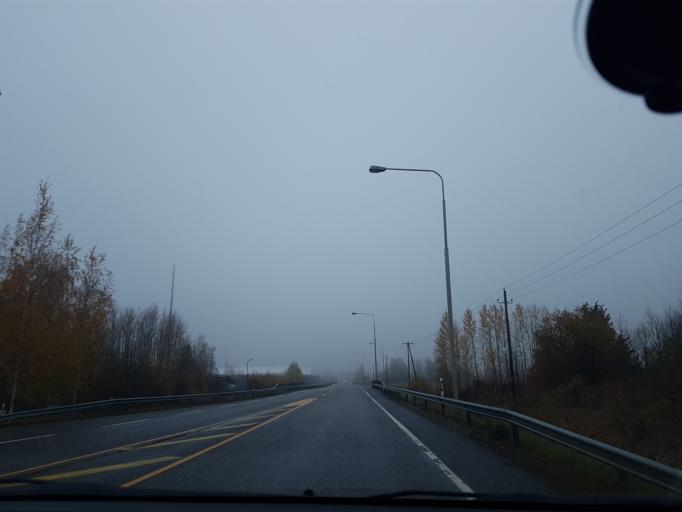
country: FI
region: Uusimaa
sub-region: Helsinki
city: Jaervenpaeae
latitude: 60.4641
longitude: 25.1398
